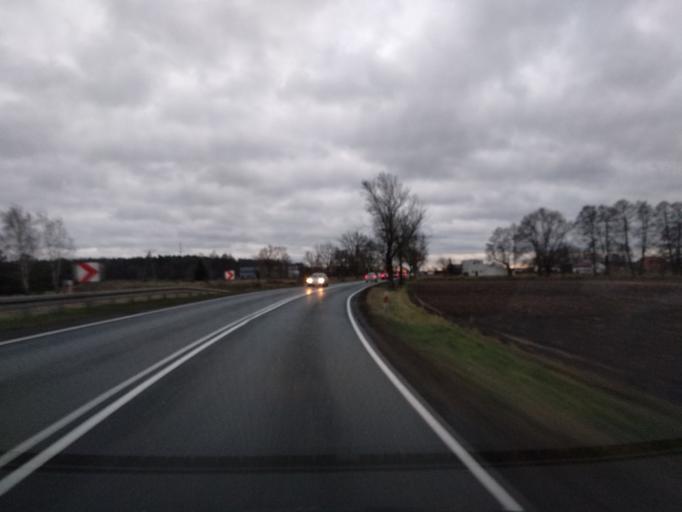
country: PL
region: Greater Poland Voivodeship
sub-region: Powiat koninski
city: Rychwal
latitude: 52.0986
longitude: 18.1675
